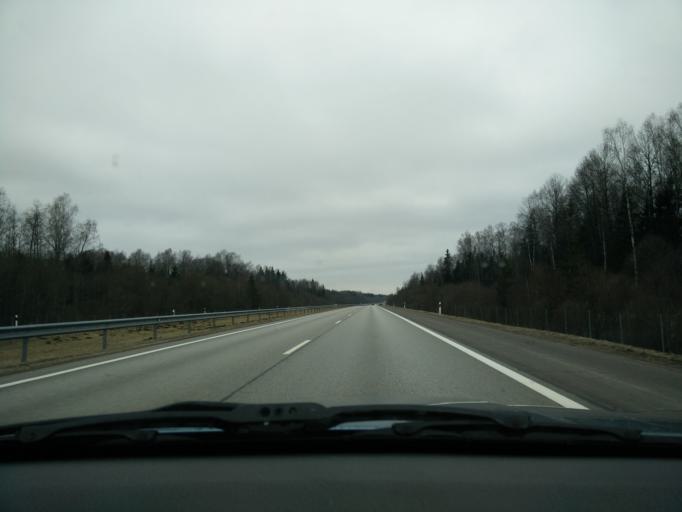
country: LT
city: Rietavas
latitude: 55.6335
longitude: 21.9361
